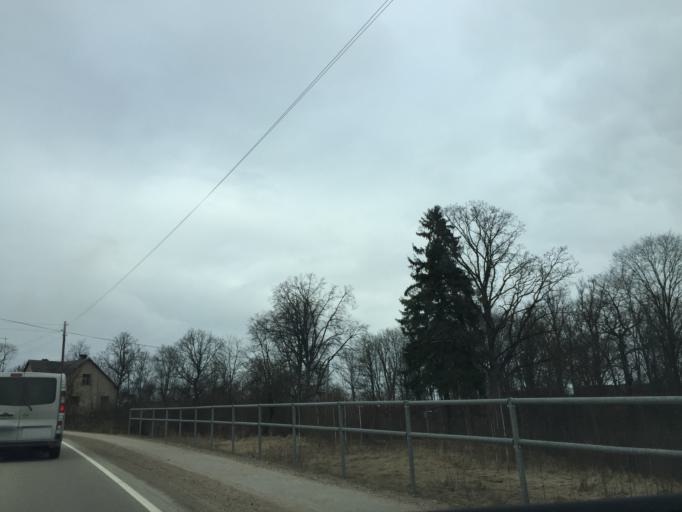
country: LV
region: Kraslavas Rajons
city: Kraslava
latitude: 55.9223
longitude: 27.1477
